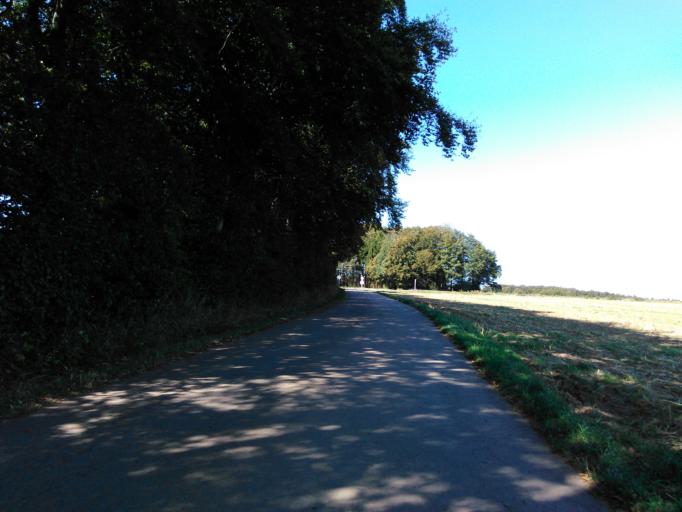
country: LU
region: Diekirch
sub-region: Canton de Redange
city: Rambrouch
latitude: 49.8089
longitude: 5.8457
